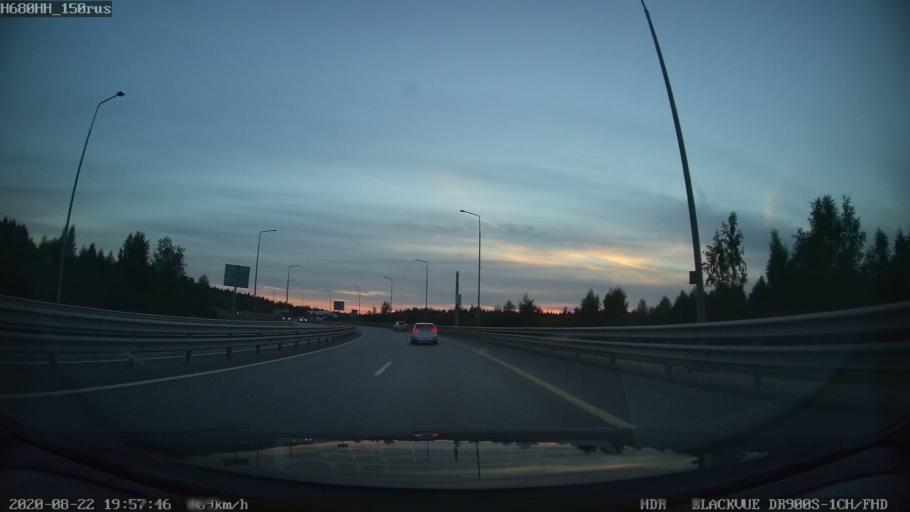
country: RU
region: Tverskaya
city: Gorodnya
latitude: 56.7362
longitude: 36.2432
